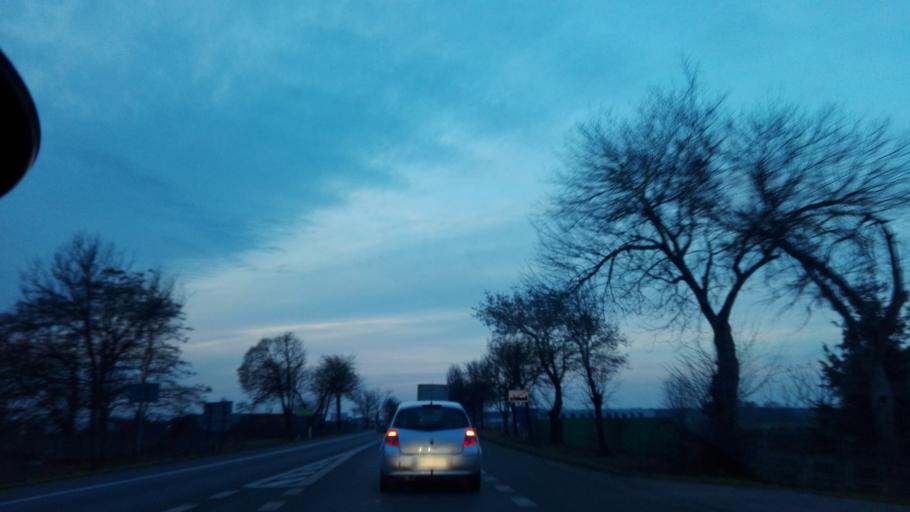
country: PL
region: Masovian Voivodeship
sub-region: Powiat siedlecki
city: Skorzec
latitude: 52.1783
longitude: 22.1766
